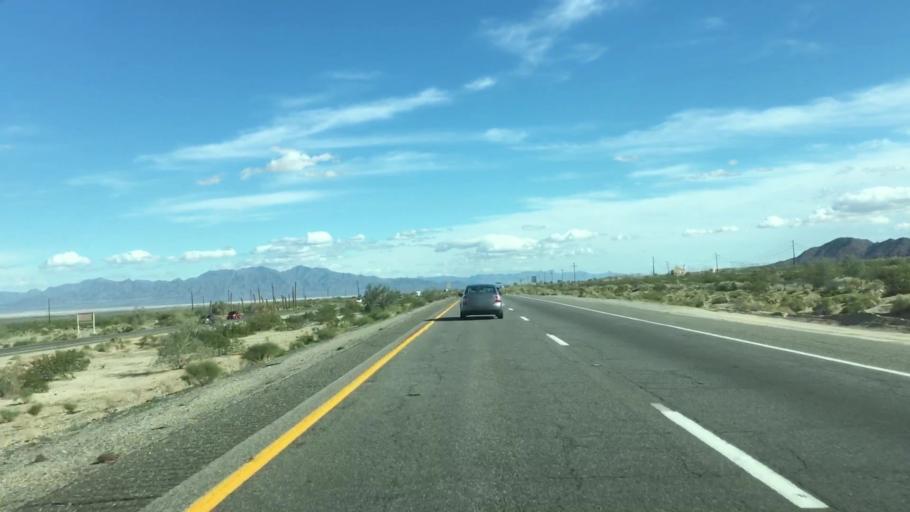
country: US
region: California
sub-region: Imperial County
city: Niland
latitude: 33.7104
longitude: -115.3923
